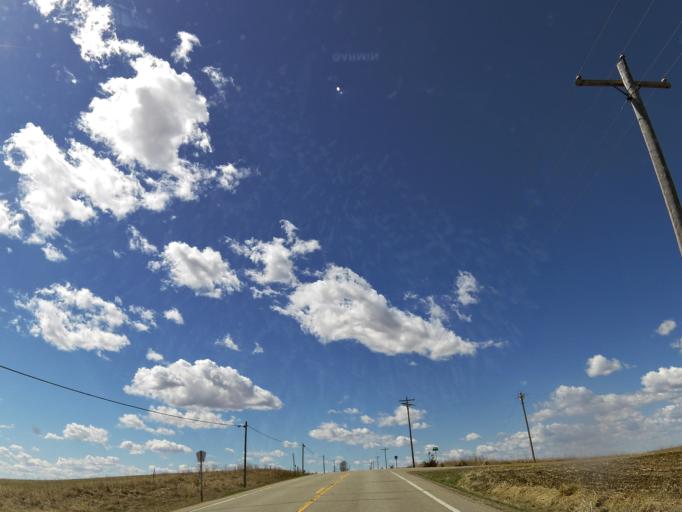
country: US
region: Minnesota
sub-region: Dakota County
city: Hastings
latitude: 44.7567
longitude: -92.9129
